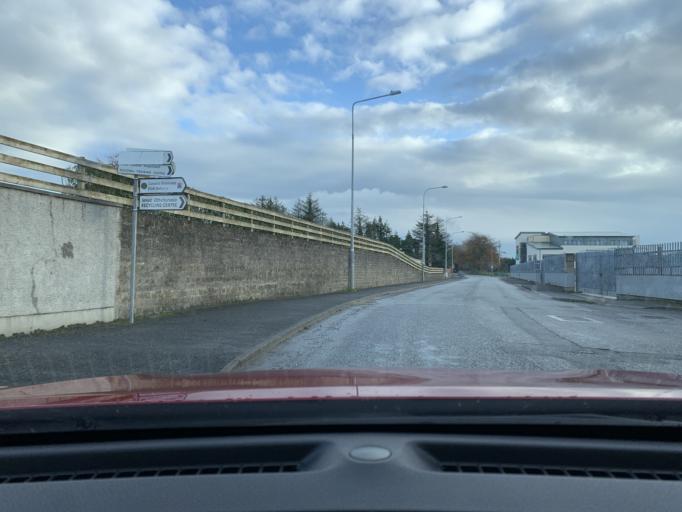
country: IE
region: Ulster
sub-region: County Donegal
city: Ballybofey
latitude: 54.8021
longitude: -7.7717
